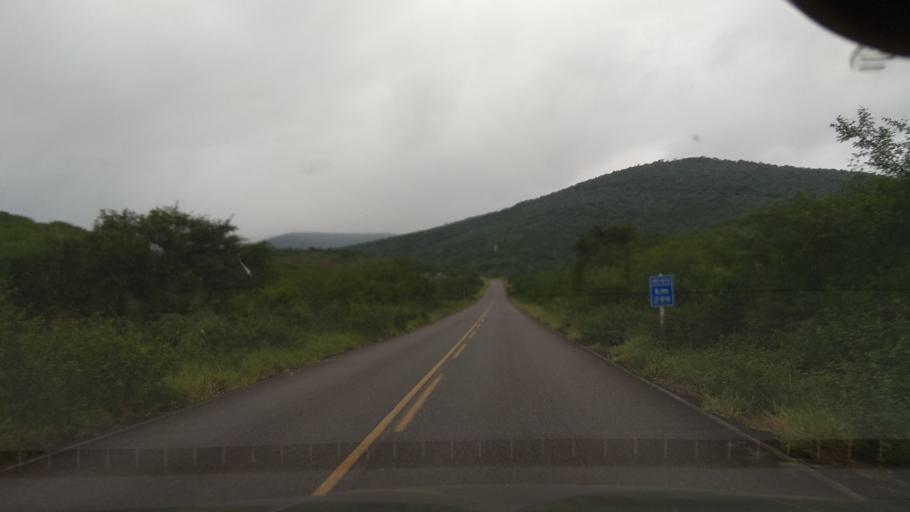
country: BR
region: Bahia
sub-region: Santa Ines
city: Santa Ines
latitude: -13.2513
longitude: -39.7716
